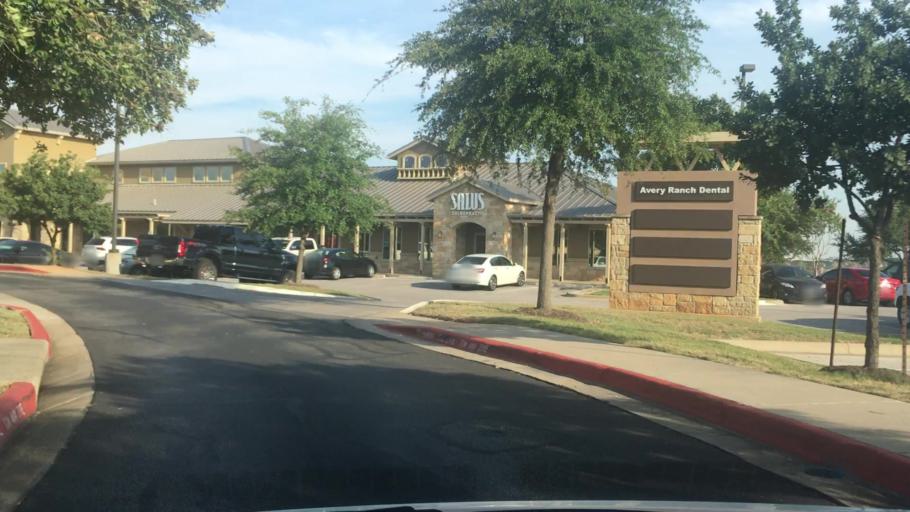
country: US
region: Texas
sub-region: Williamson County
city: Brushy Creek
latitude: 30.4994
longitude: -97.7744
